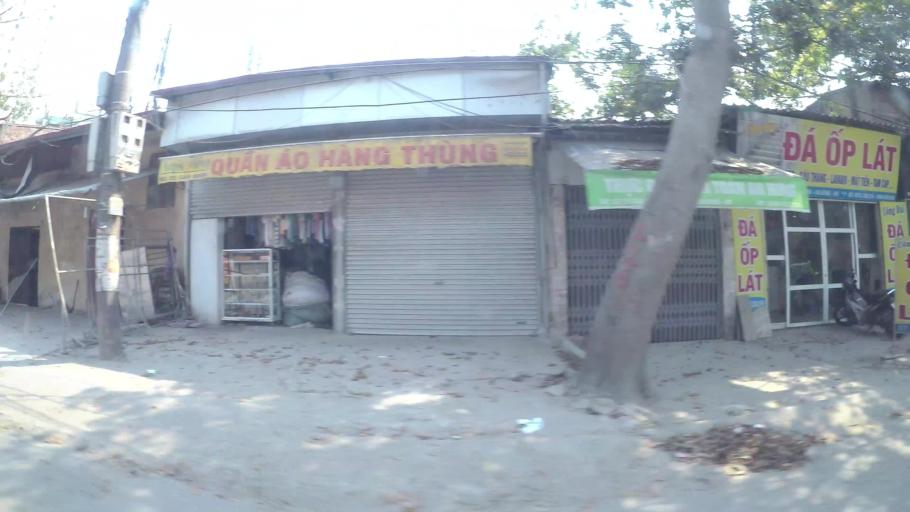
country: VN
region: Ha Noi
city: Ha Dong
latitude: 20.9592
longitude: 105.8039
